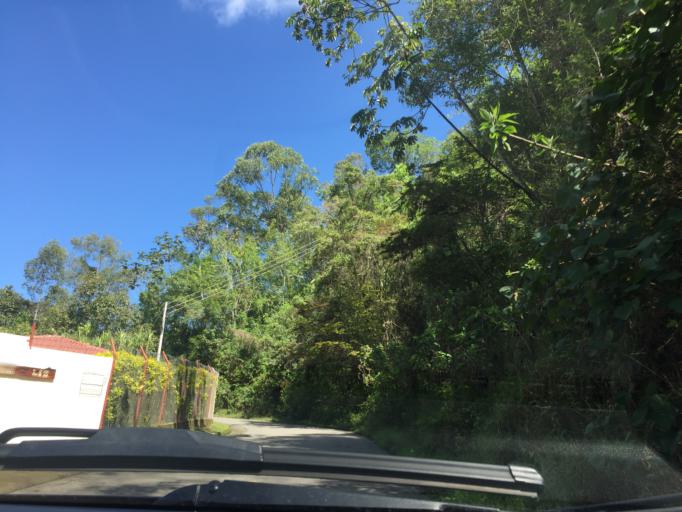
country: CO
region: Cundinamarca
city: San Francisco
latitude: 4.9989
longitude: -74.2821
